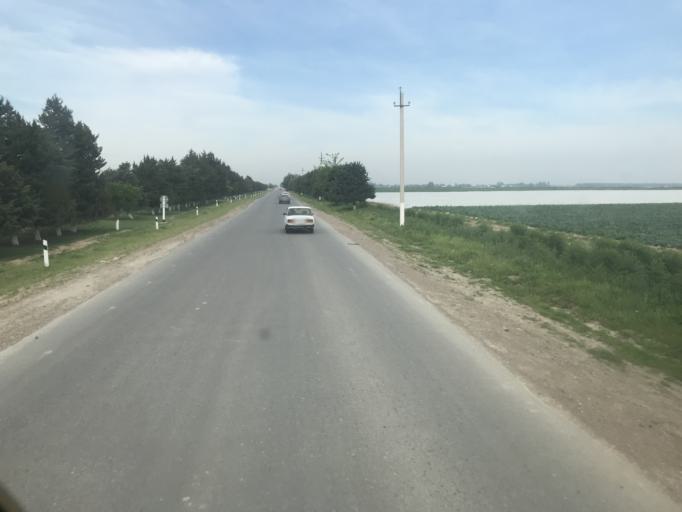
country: KZ
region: Ongtustik Qazaqstan
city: Asykata
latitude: 40.9849
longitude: 68.2940
